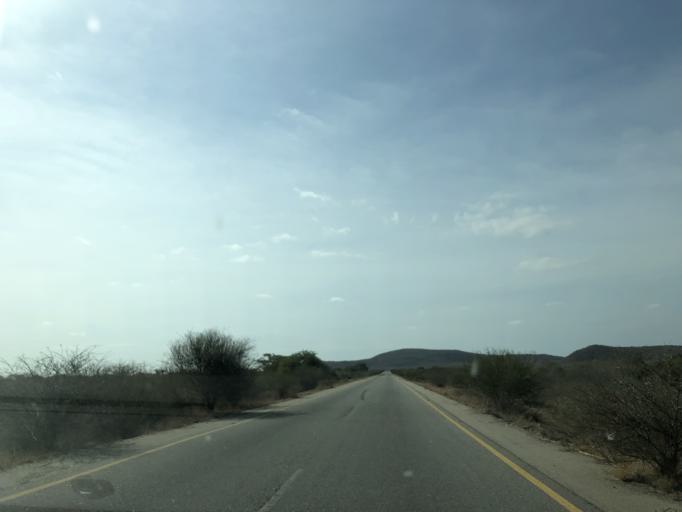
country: AO
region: Benguela
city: Benguela
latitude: -12.9080
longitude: 13.5080
